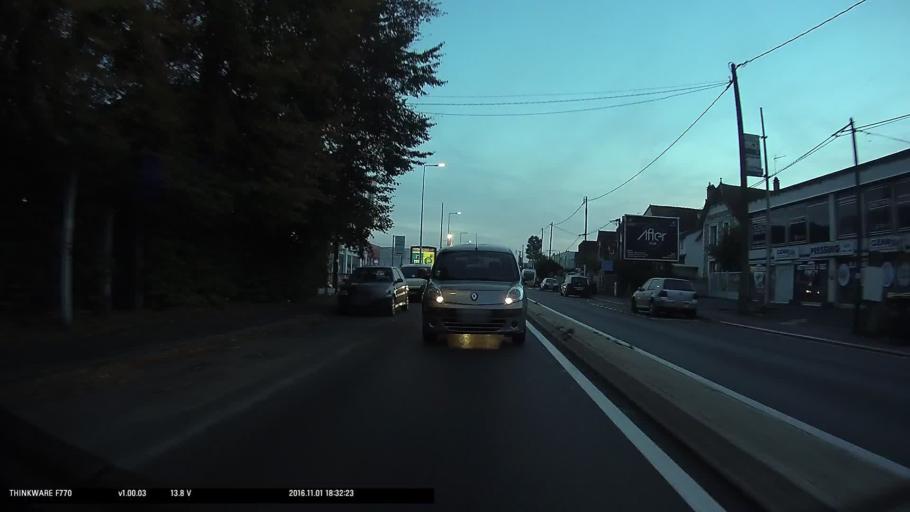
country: FR
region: Ile-de-France
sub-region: Departement de l'Essonne
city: Villemoisson-sur-Orge
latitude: 48.6536
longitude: 2.3379
